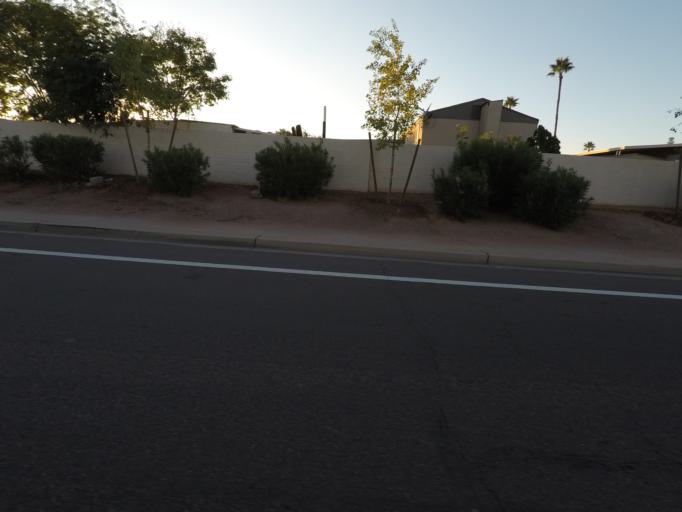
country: US
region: Arizona
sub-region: Maricopa County
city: Guadalupe
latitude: 33.3792
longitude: -111.9439
